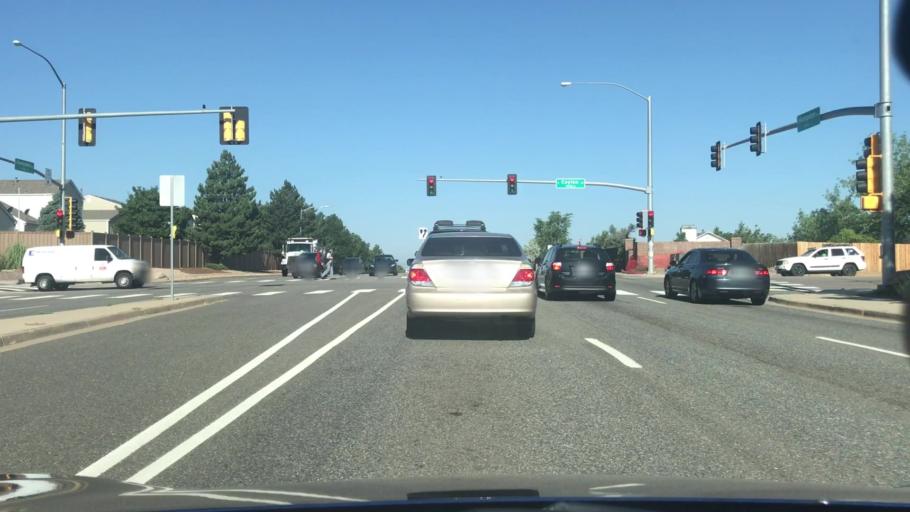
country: US
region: Colorado
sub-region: Arapahoe County
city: Dove Valley
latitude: 39.6530
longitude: -104.7633
